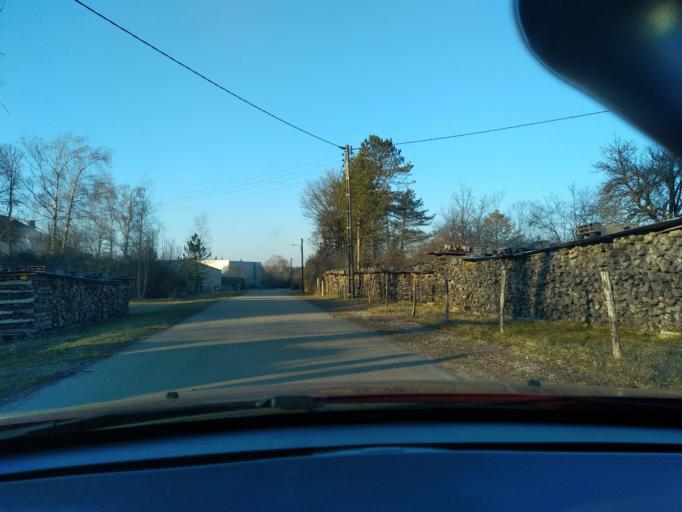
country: FR
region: Franche-Comte
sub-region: Departement du Jura
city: Clairvaux-les-Lacs
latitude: 46.5768
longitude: 5.6907
